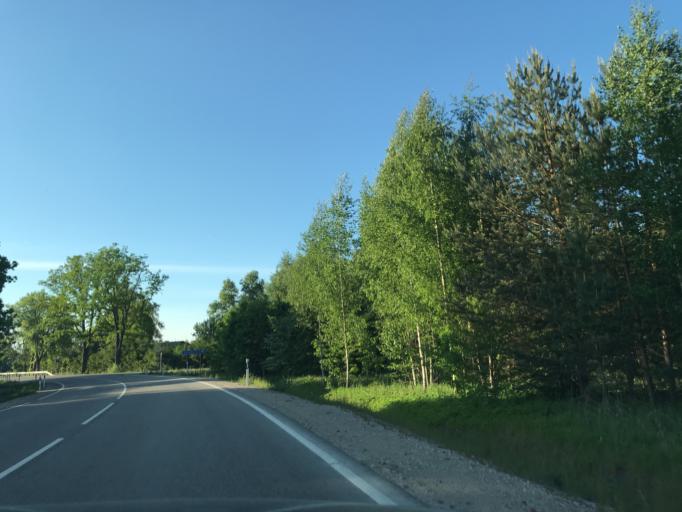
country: LV
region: Ozolnieku
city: Ozolnieki
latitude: 56.6096
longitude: 23.7892
